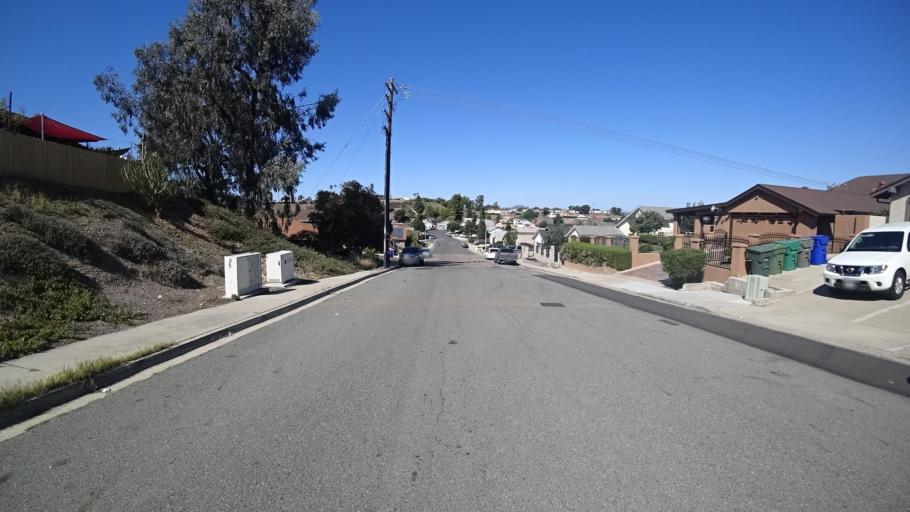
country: US
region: California
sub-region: San Diego County
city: La Presa
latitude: 32.6990
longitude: -117.0233
